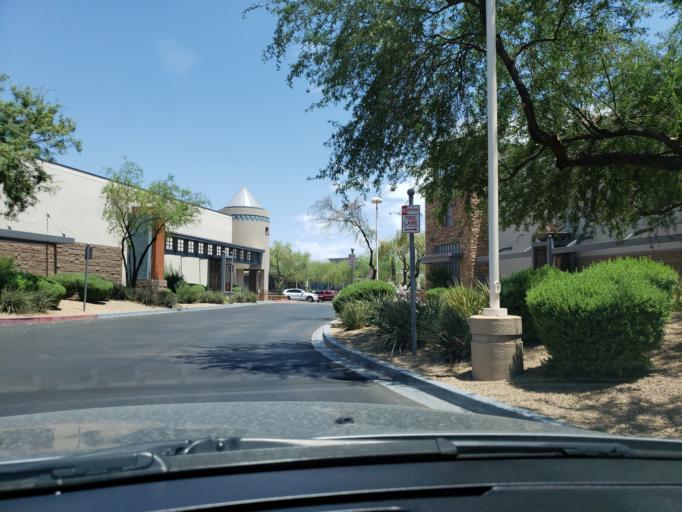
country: US
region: Arizona
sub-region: Maricopa County
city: Paradise Valley
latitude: 33.6336
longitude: -111.9236
